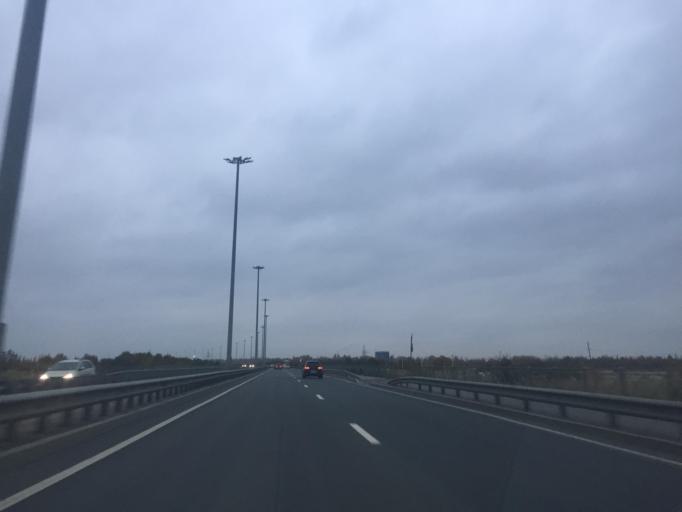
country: RU
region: St.-Petersburg
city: Shushary
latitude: 59.7654
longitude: 30.3987
